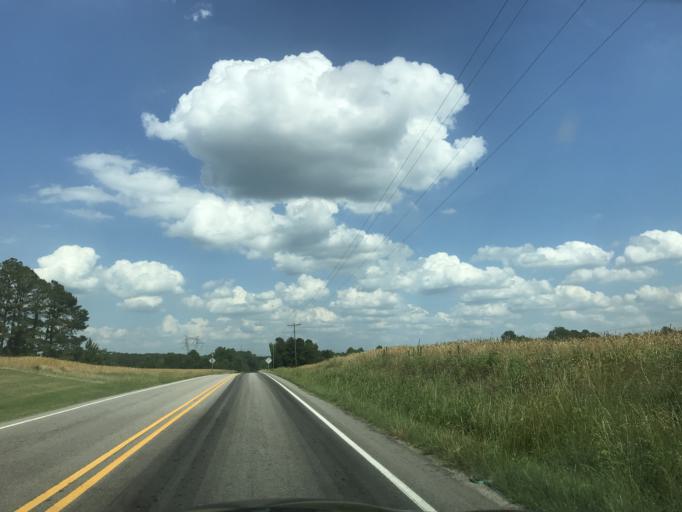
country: US
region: North Carolina
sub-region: Franklin County
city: Louisburg
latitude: 35.9620
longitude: -78.2908
